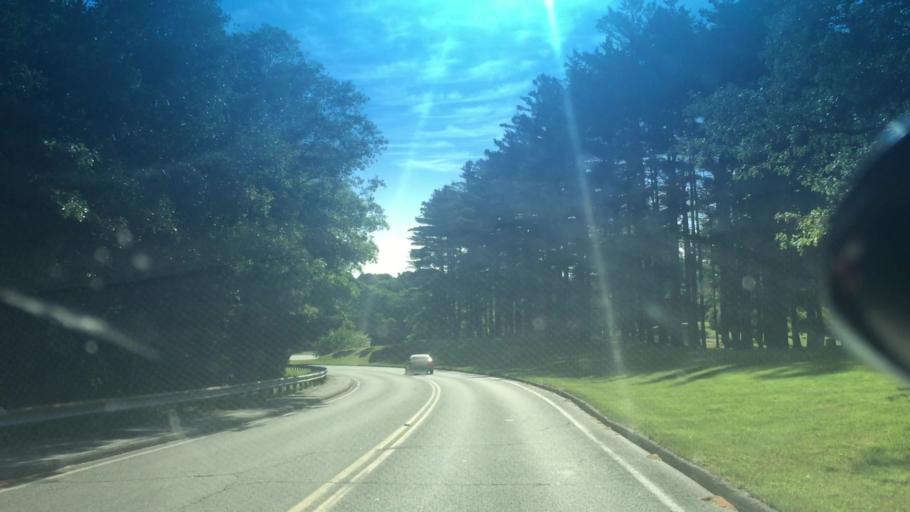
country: US
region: Massachusetts
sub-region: Norfolk County
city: Medfield
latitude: 42.1882
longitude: -71.3158
